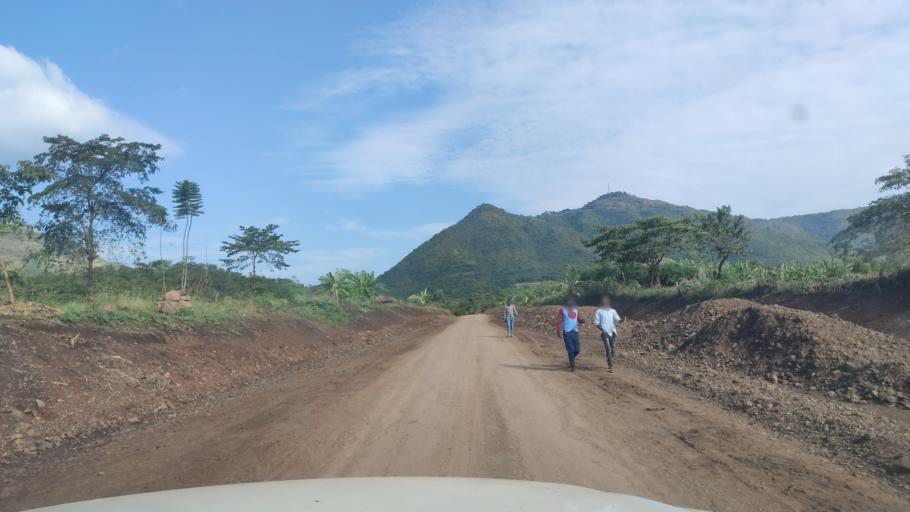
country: ET
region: Southern Nations, Nationalities, and People's Region
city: Arba Minch'
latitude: 6.4271
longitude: 37.3283
